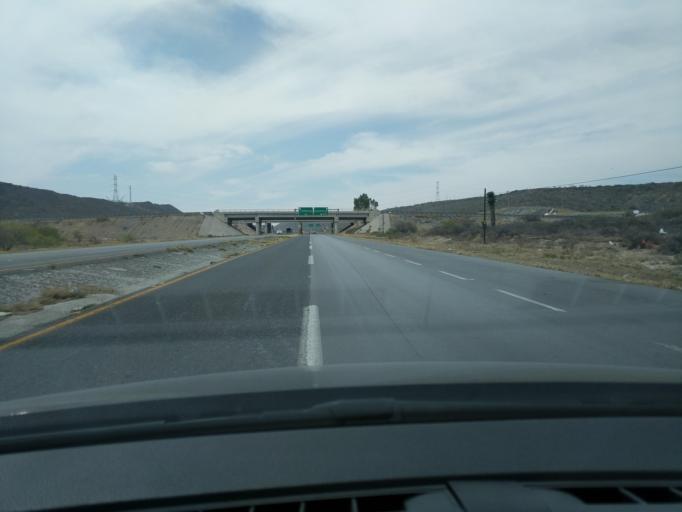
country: MX
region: Coahuila
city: Saltillo
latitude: 25.4535
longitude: -101.0626
